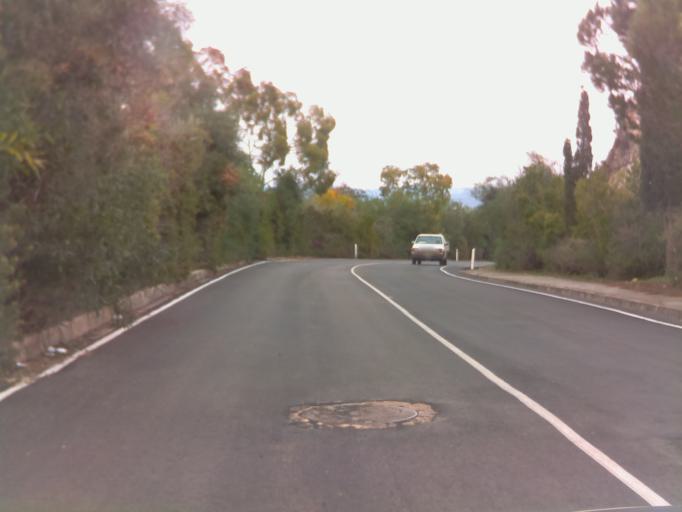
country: CY
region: Pafos
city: Polis
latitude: 35.0427
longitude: 32.3714
